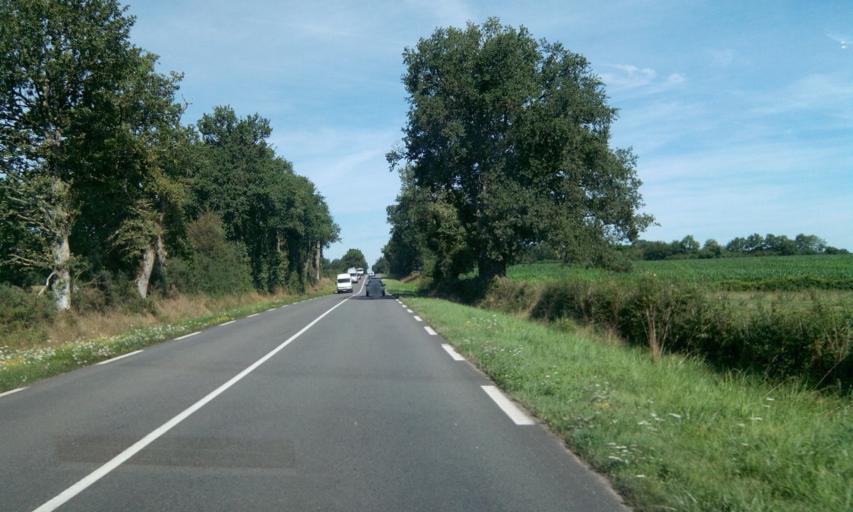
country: FR
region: Poitou-Charentes
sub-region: Departement de la Charente
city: Confolens
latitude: 46.0466
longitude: 0.6220
